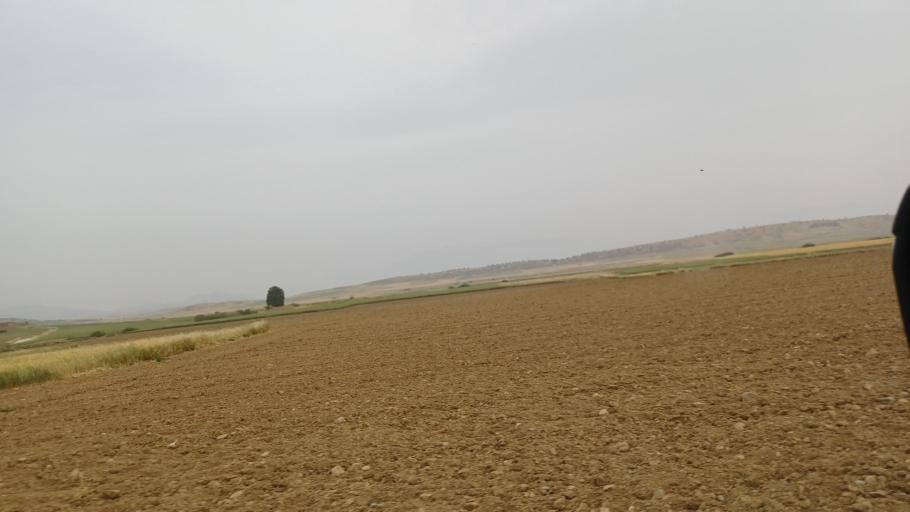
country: CY
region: Lefkosia
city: Mammari
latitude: 35.1844
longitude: 33.1703
